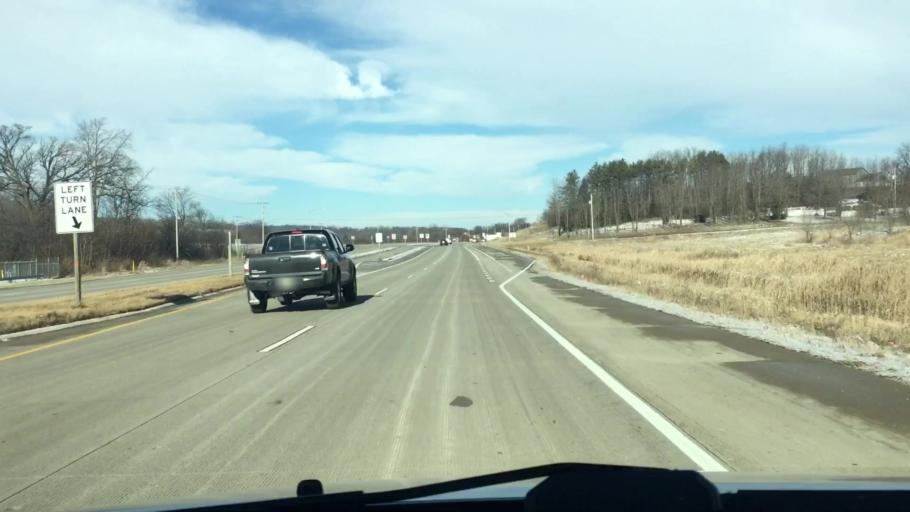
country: US
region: Wisconsin
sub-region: Waukesha County
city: Mukwonago
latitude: 42.8988
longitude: -88.3444
